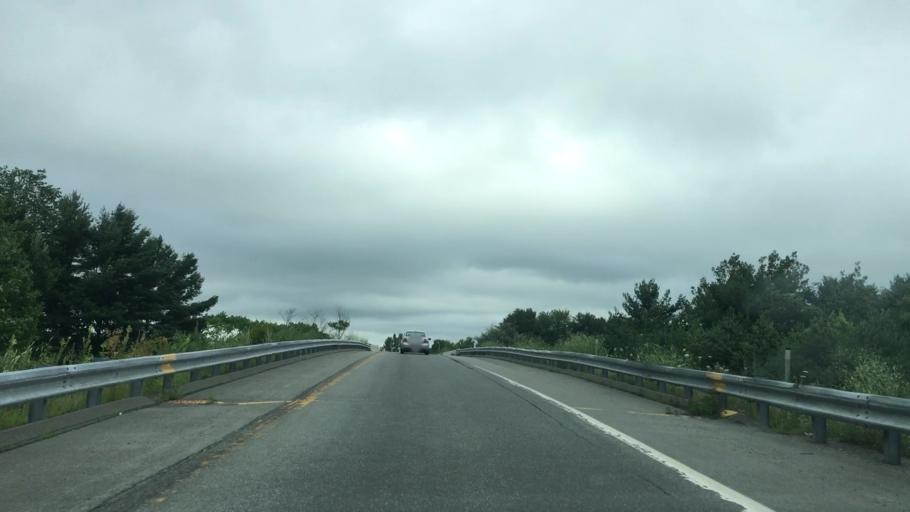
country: US
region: Maine
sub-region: Penobscot County
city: Brewer
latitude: 44.8243
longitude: -68.7539
